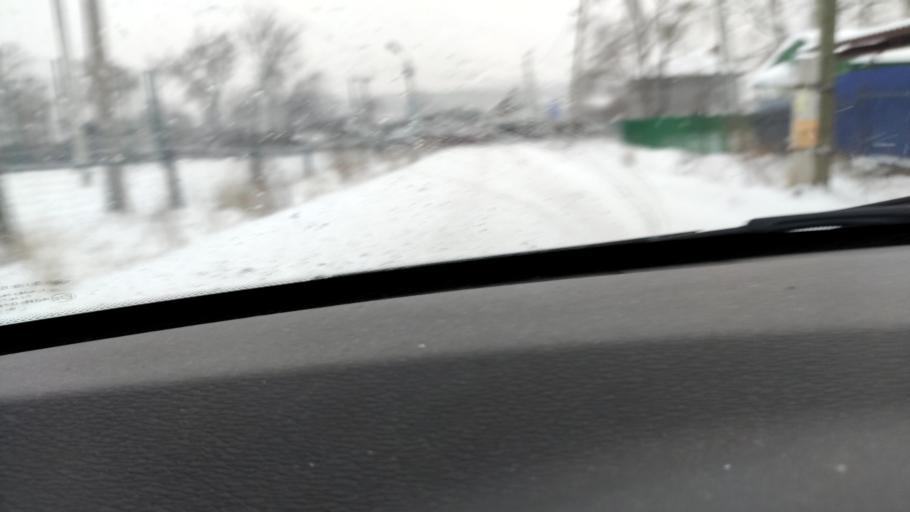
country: RU
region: Perm
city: Ust'-Kachka
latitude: 57.9409
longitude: 55.7425
